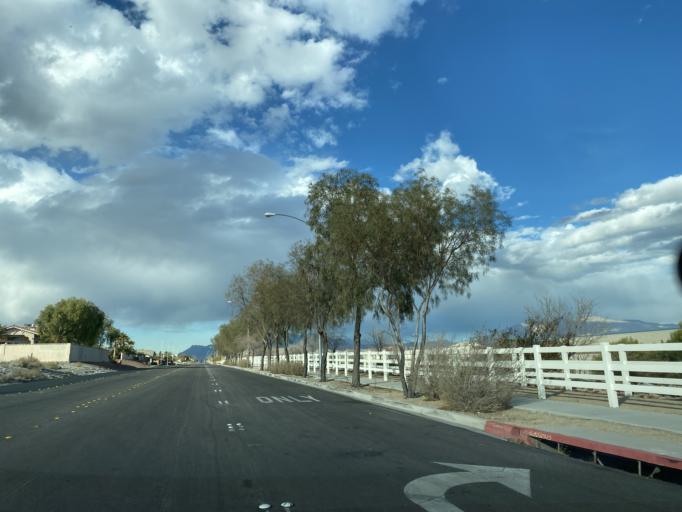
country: US
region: Nevada
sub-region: Clark County
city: Summerlin South
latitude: 36.2812
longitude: -115.3058
